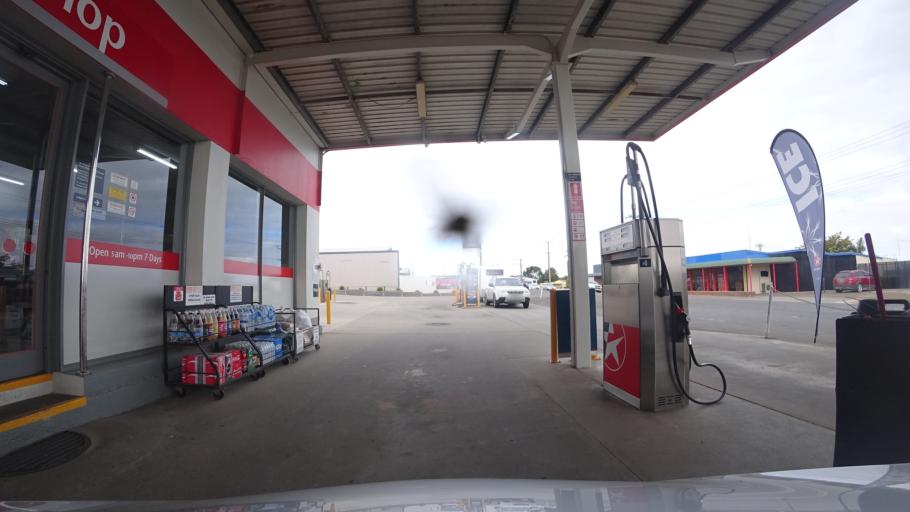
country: AU
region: South Australia
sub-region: Kangaroo Island
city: Kingscote
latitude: -35.6529
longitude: 137.6357
